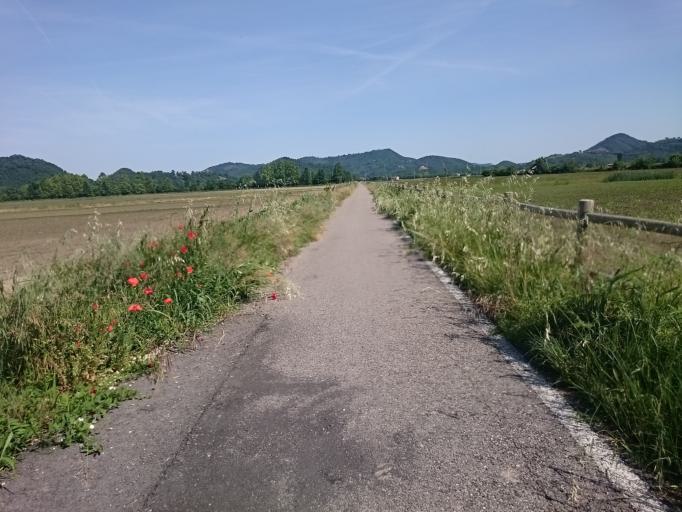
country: IT
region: Veneto
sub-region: Provincia di Padova
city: Montemerlo
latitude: 45.3781
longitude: 11.6853
